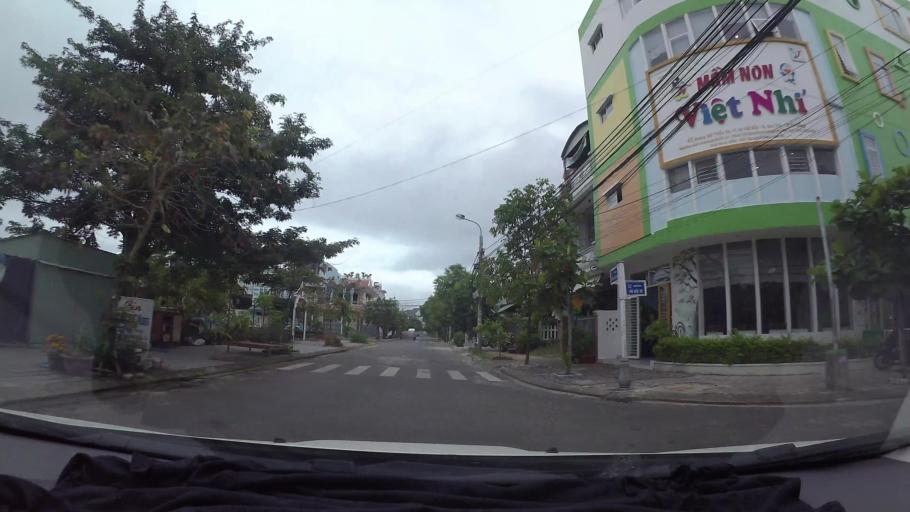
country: VN
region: Da Nang
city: Da Nang
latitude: 16.0850
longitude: 108.2344
